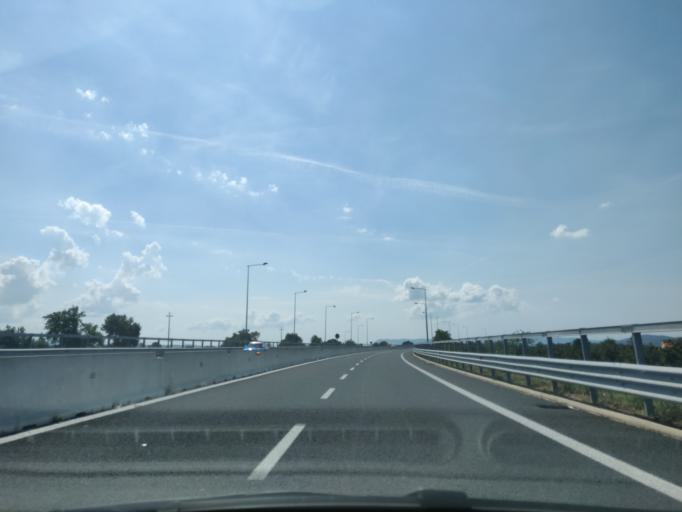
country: IT
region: Latium
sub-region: Provincia di Viterbo
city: Blera
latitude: 42.3107
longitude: 11.9920
